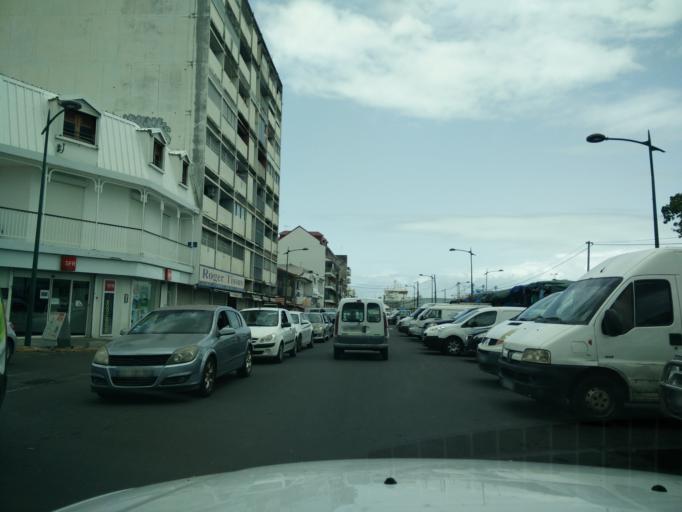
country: GP
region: Guadeloupe
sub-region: Guadeloupe
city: Pointe-a-Pitre
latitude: 16.2412
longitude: -61.5381
